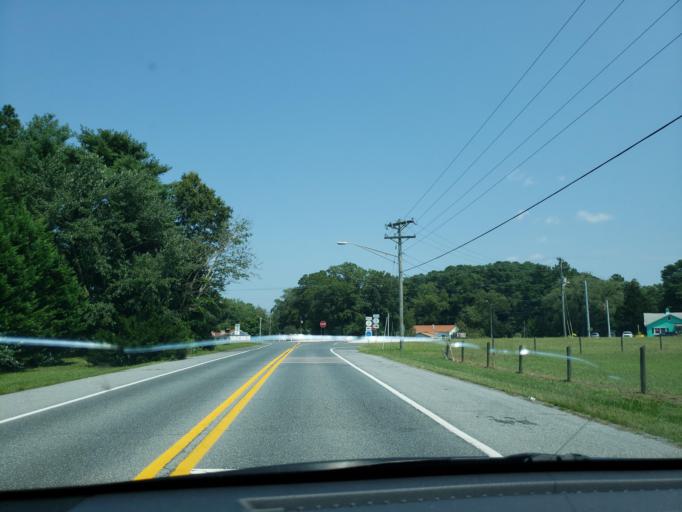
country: US
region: Delaware
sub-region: Sussex County
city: Milton
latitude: 38.8206
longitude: -75.3071
